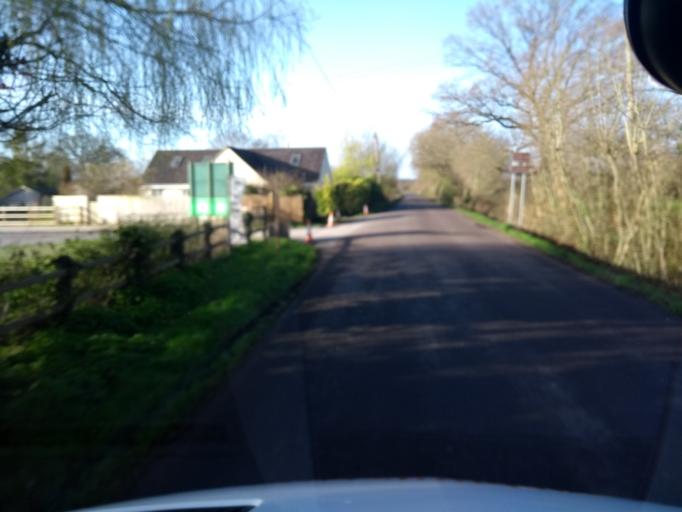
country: GB
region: England
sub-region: Somerset
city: Wedmore
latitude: 51.1697
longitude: -2.8228
